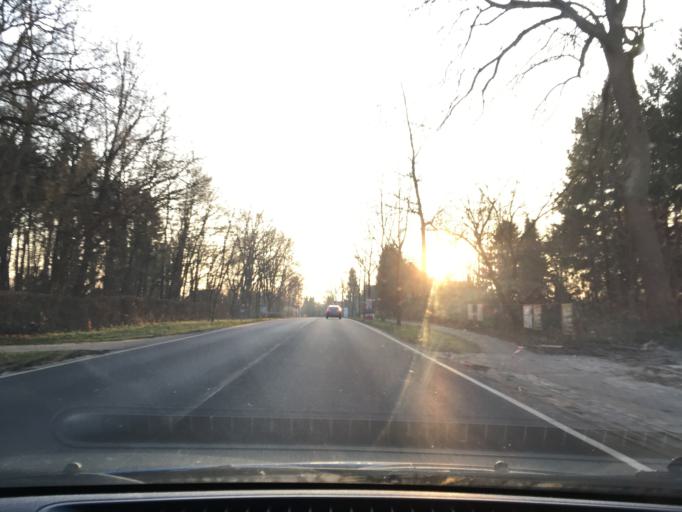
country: DE
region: Lower Saxony
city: Eschede
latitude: 52.7419
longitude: 10.2443
